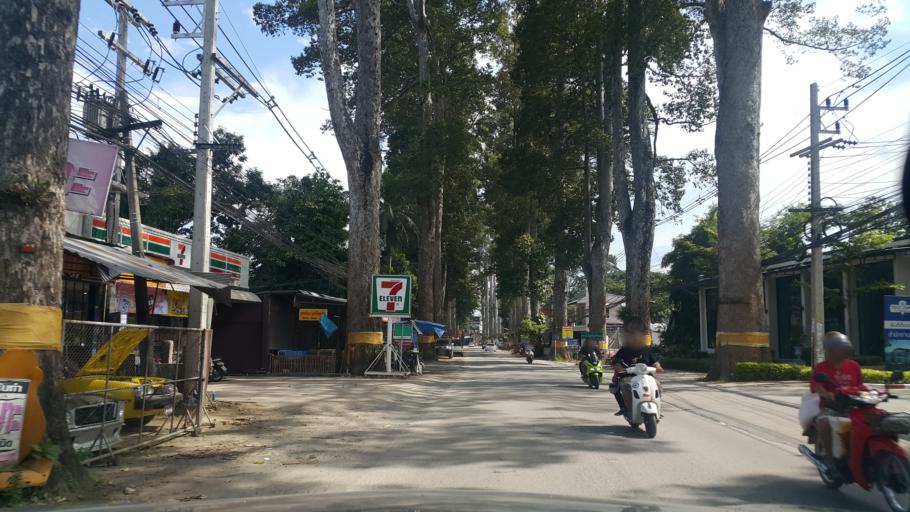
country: TH
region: Chiang Mai
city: Saraphi
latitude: 18.7370
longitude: 99.0155
